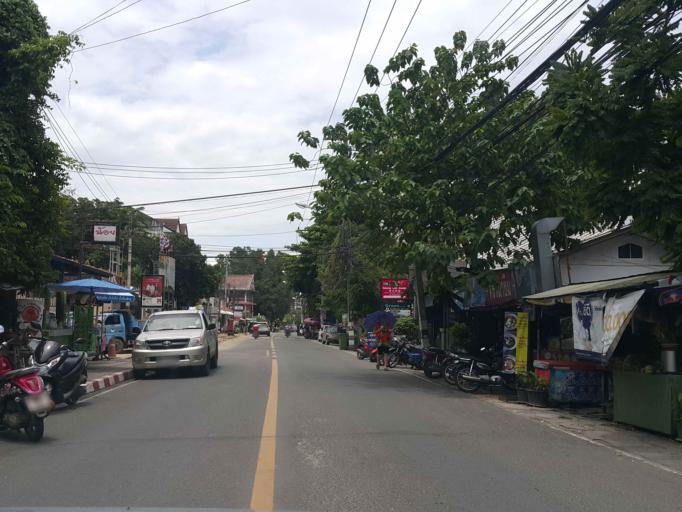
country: TH
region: Chiang Mai
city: Chiang Mai
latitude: 18.7911
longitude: 98.9822
